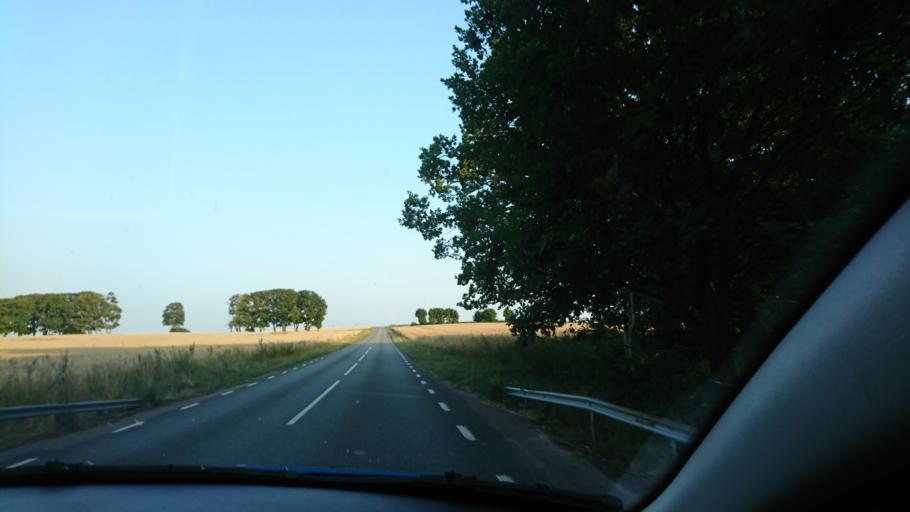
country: SE
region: Skane
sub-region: Simrishamns Kommun
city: Kivik
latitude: 55.7006
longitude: 14.1515
